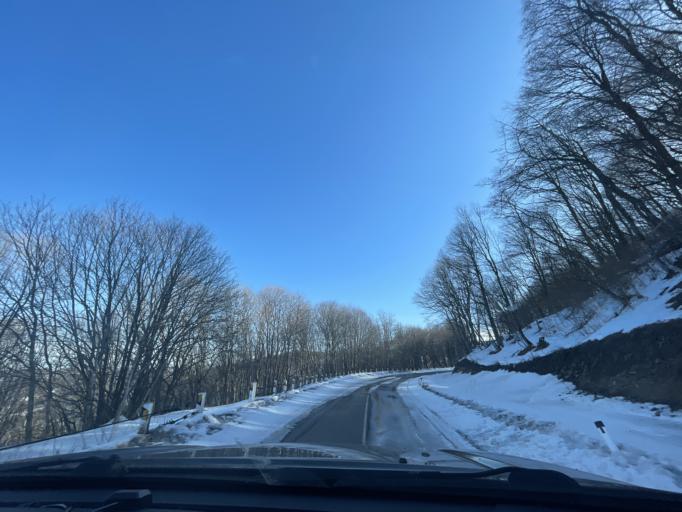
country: GE
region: Kvemo Kartli
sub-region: Tetri Tsqaro
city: Manglisi
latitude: 41.7693
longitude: 44.5076
